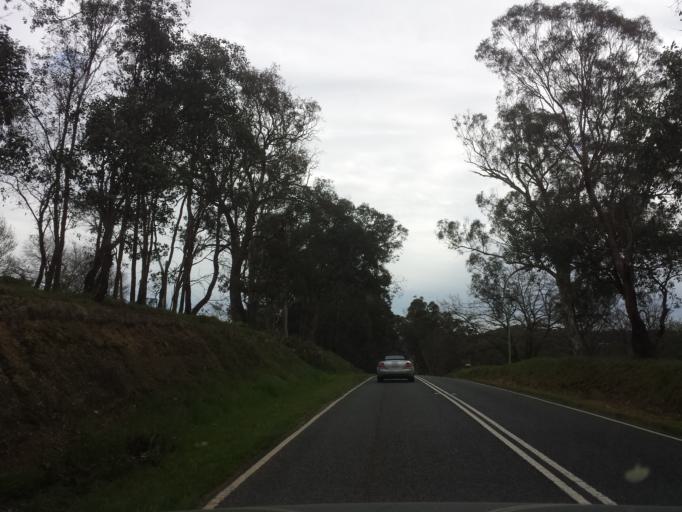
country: AU
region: Victoria
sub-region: Yarra Ranges
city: Yarra Glen
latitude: -37.6493
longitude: 145.3241
